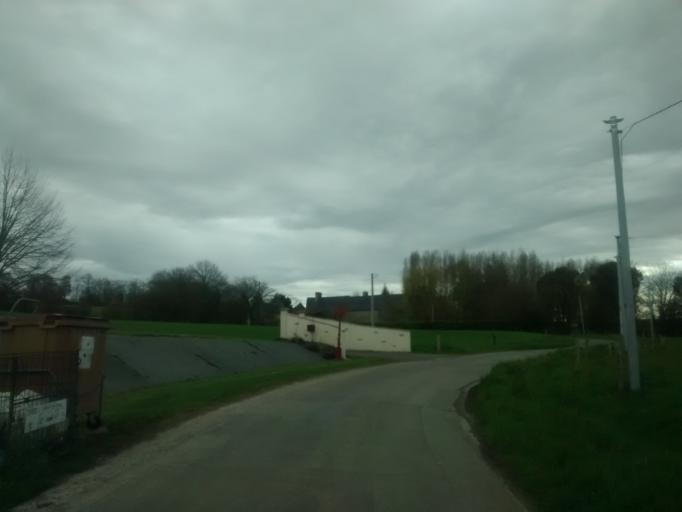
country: FR
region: Brittany
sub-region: Departement d'Ille-et-Vilaine
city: Gosne
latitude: 48.2467
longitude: -1.4802
